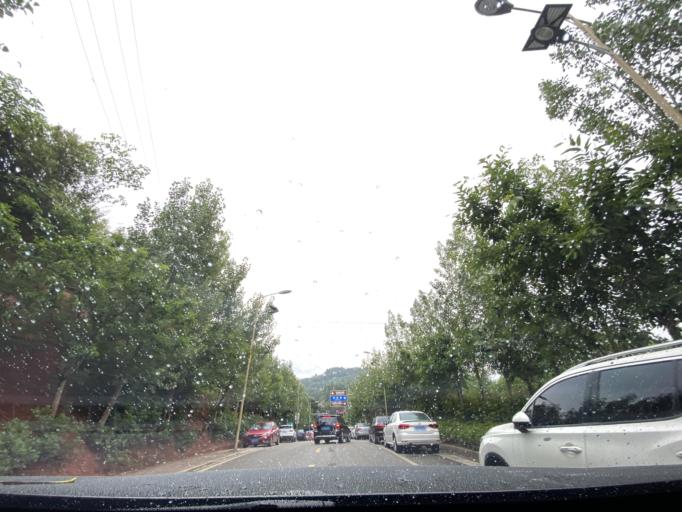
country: CN
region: Sichuan
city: Longquan
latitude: 30.6066
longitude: 104.4762
